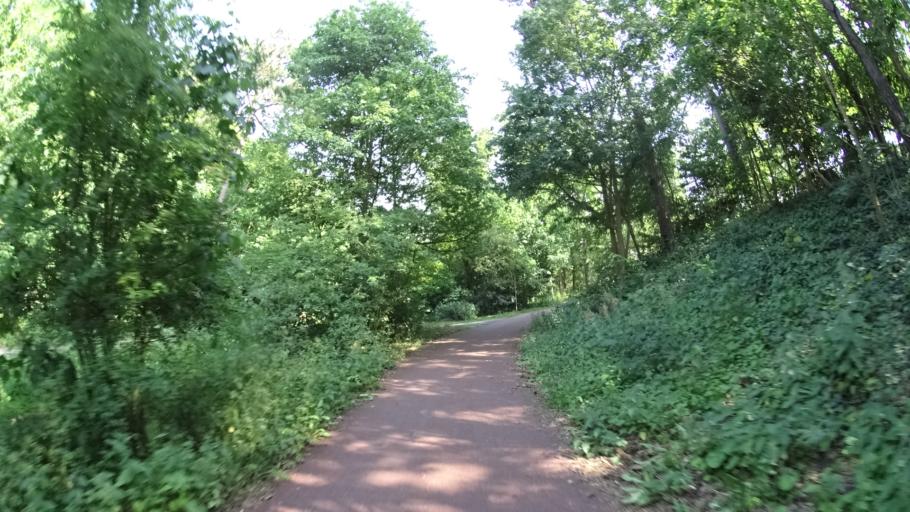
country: NL
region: South Holland
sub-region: Gemeente Den Haag
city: Scheveningen
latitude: 52.1041
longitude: 4.2987
